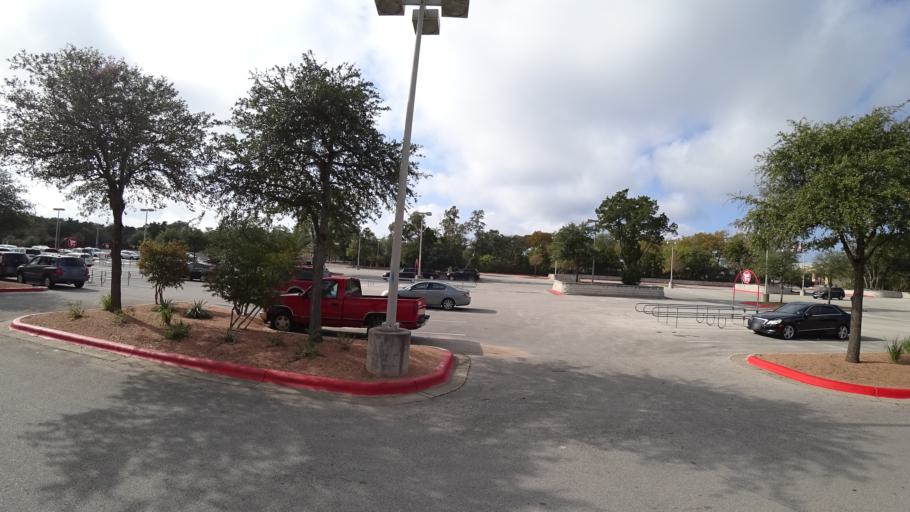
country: US
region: Texas
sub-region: Williamson County
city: Anderson Mill
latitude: 30.4026
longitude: -97.8508
